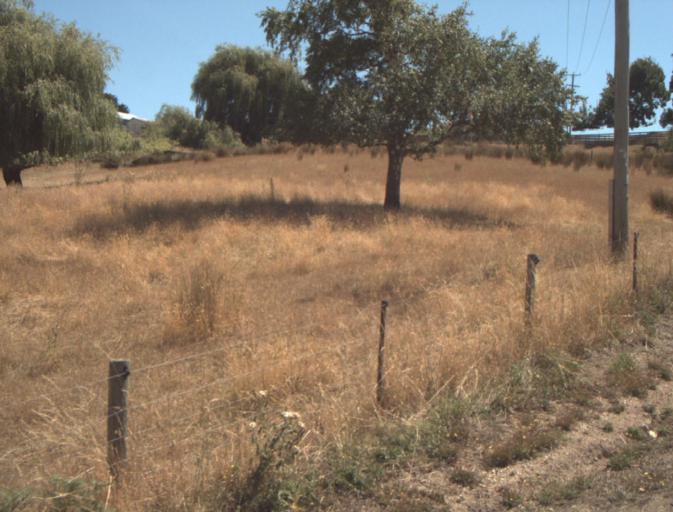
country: AU
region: Tasmania
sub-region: Launceston
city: Mayfield
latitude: -41.2501
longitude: 147.1342
